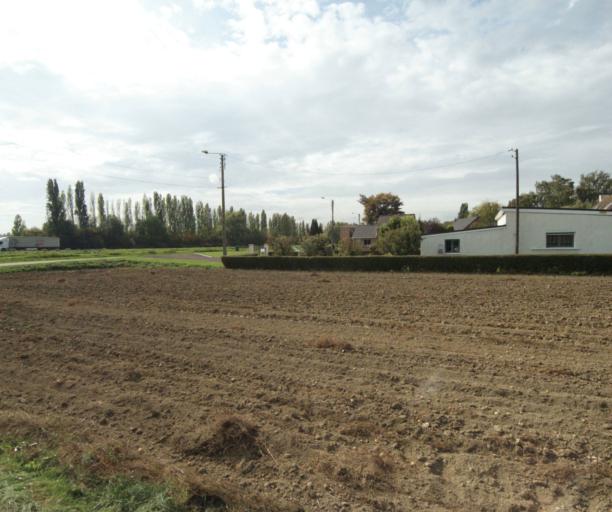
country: FR
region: Nord-Pas-de-Calais
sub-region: Departement du Nord
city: Salome
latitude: 50.5287
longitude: 2.8471
